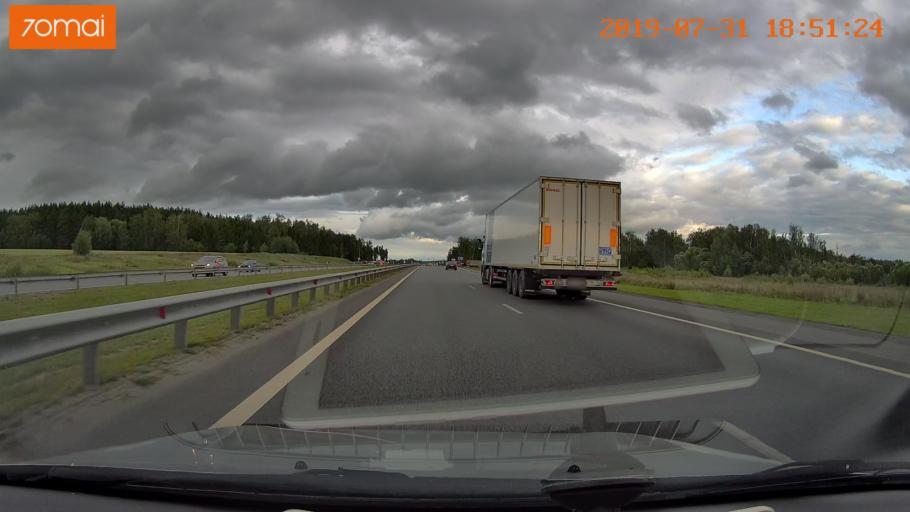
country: RU
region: Moskovskaya
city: Voskresensk
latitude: 55.2220
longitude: 38.6059
